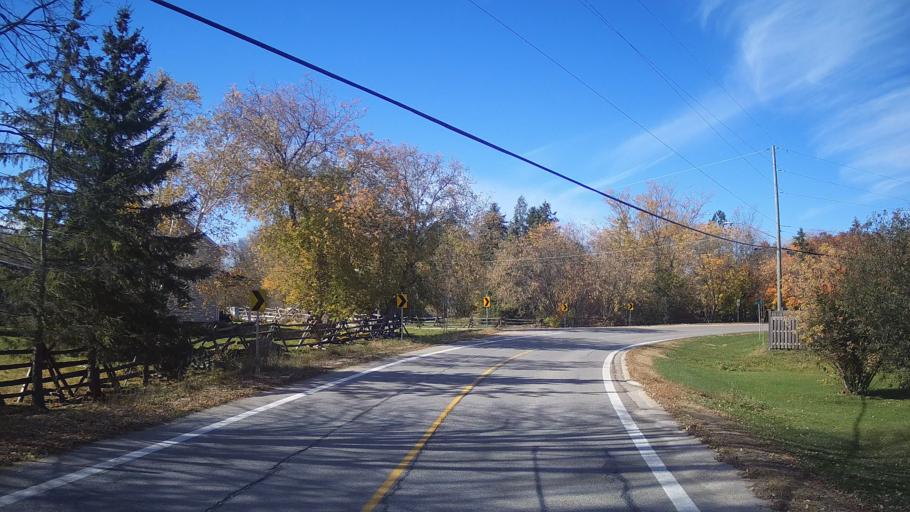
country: CA
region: Ontario
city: Perth
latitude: 44.8753
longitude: -76.3028
